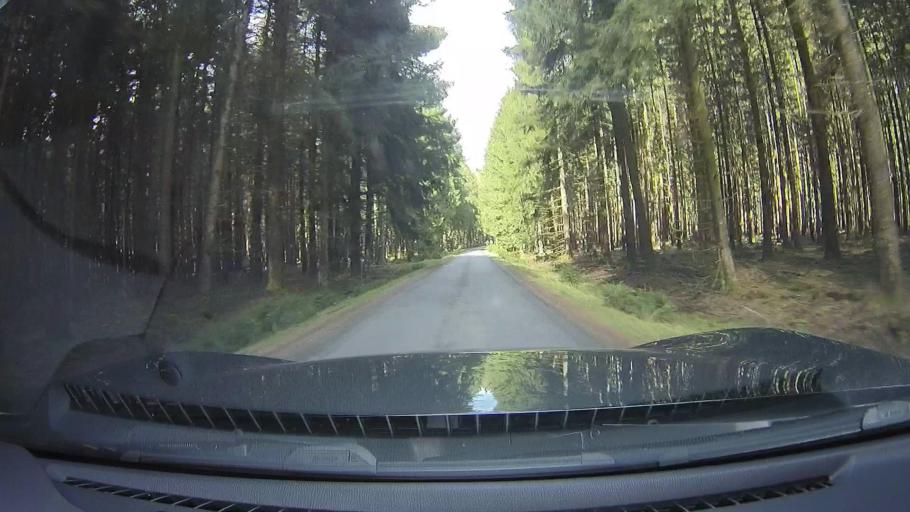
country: DE
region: Hesse
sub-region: Regierungsbezirk Darmstadt
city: Hesseneck
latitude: 49.6092
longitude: 9.0790
